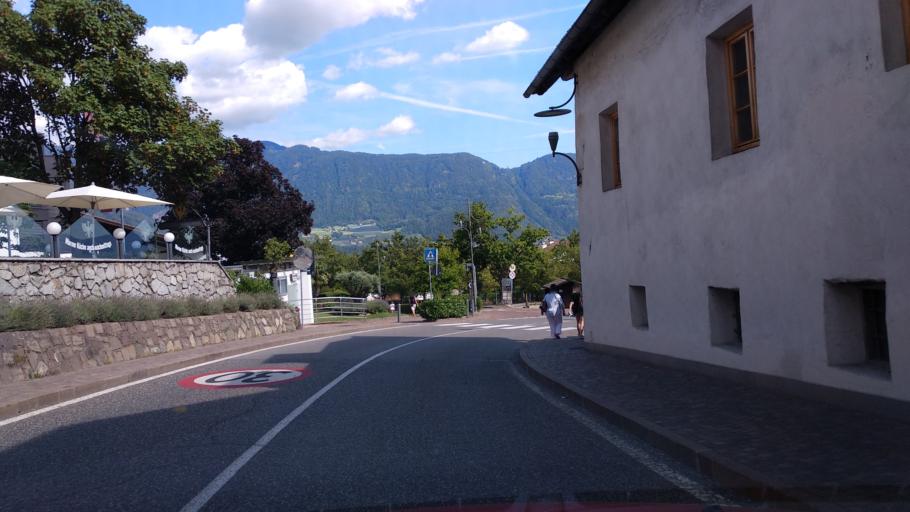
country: IT
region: Trentino-Alto Adige
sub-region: Bolzano
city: Tirolo
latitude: 46.6892
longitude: 11.1559
